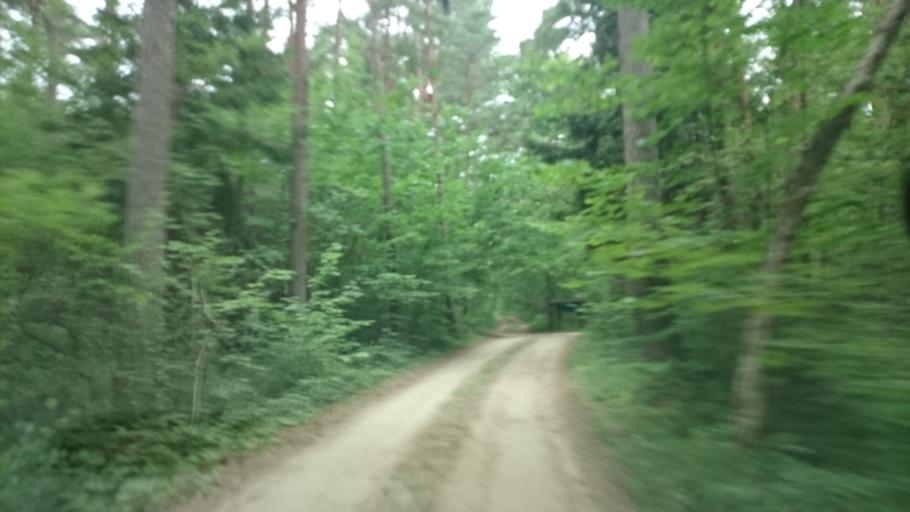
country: EE
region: Saare
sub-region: Orissaare vald
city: Orissaare
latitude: 58.5955
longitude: 22.6962
